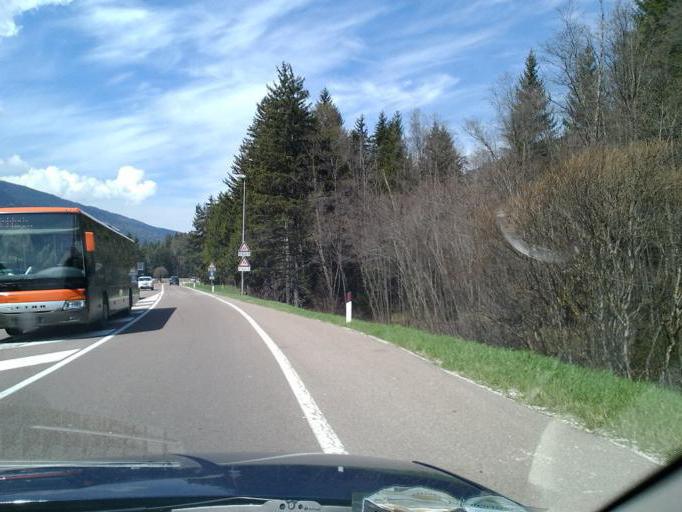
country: IT
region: Trentino-Alto Adige
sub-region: Bolzano
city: Villabassa
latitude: 46.7386
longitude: 12.1556
